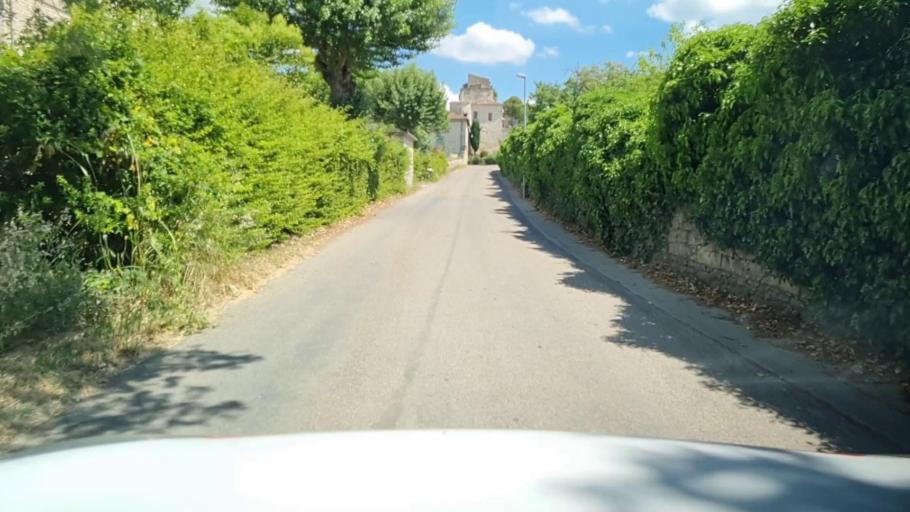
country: FR
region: Languedoc-Roussillon
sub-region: Departement du Gard
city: Saint-Mamert-du-Gard
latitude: 43.8984
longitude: 4.2127
